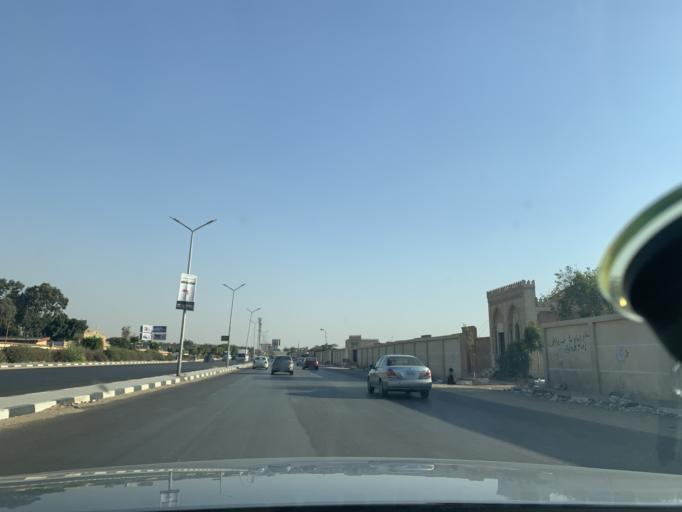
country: EG
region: Muhafazat al Qahirah
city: Cairo
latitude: 30.0292
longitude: 31.3541
